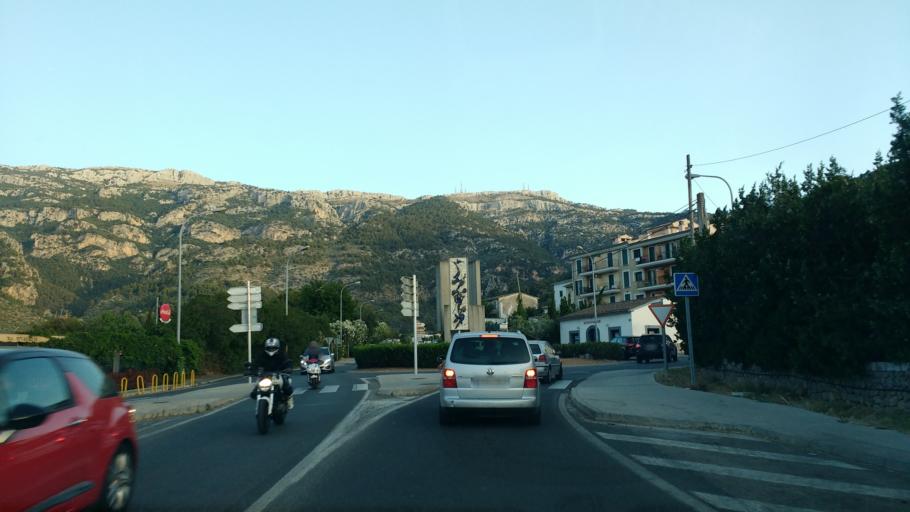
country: ES
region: Balearic Islands
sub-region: Illes Balears
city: Soller
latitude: 39.7715
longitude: 2.7060
